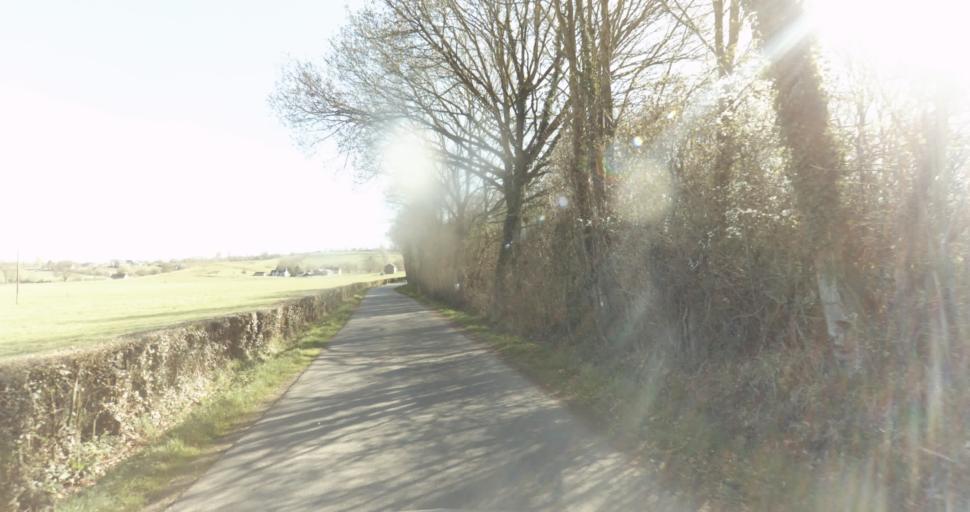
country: FR
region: Lower Normandy
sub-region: Departement du Calvados
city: Saint-Pierre-sur-Dives
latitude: 49.0275
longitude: 0.0559
